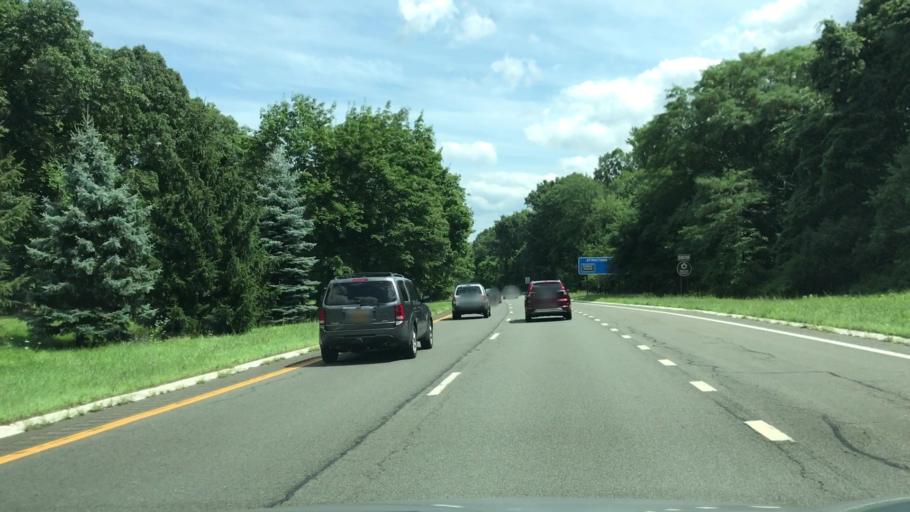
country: US
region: New York
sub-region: Rockland County
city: Orangeburg
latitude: 41.0408
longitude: -73.9550
